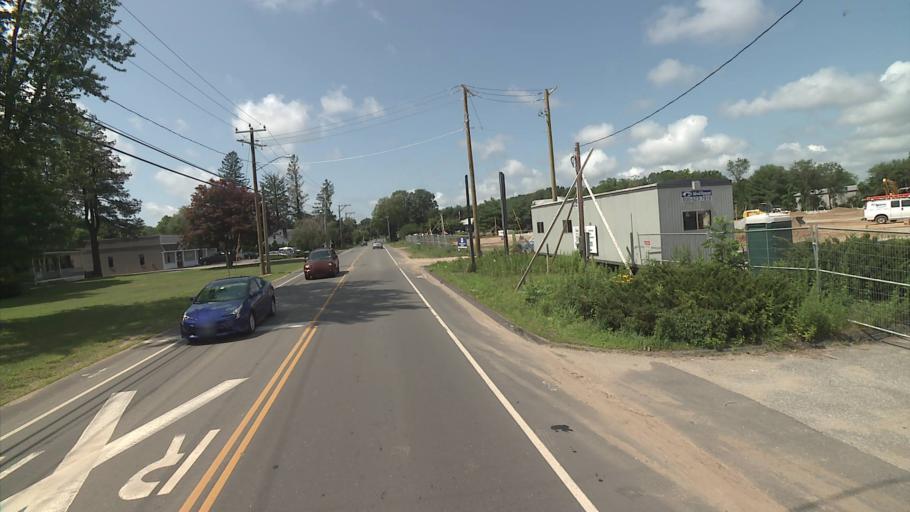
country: US
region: Connecticut
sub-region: Middlesex County
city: Essex Village
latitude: 41.3479
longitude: -72.4061
